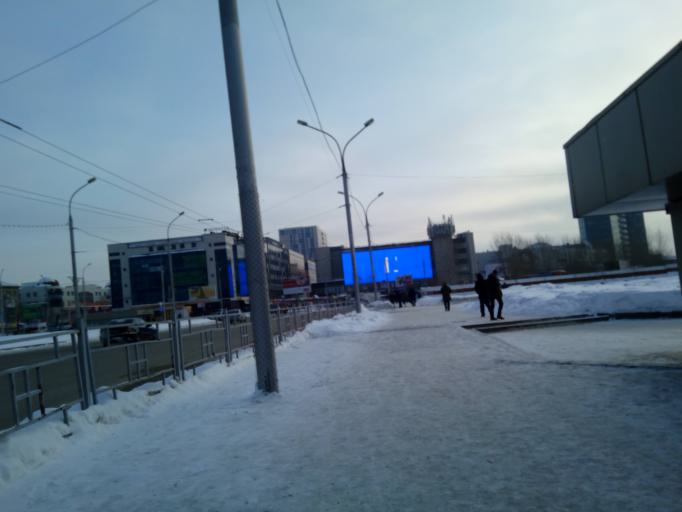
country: RU
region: Novosibirsk
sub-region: Novosibirskiy Rayon
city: Novosibirsk
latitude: 54.9829
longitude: 82.8949
